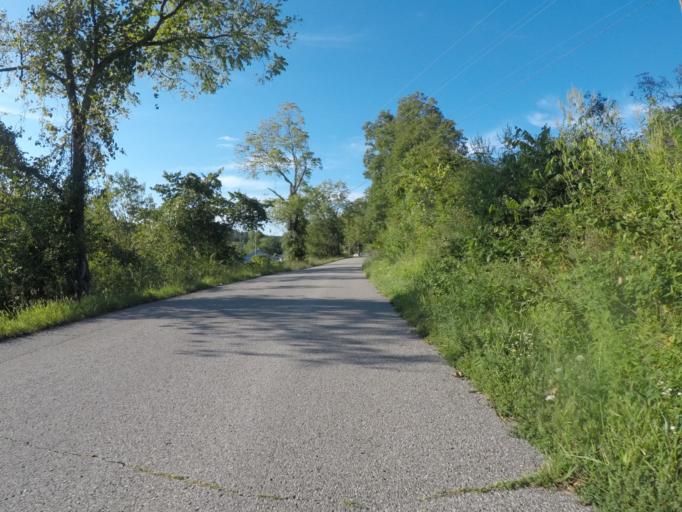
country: US
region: West Virginia
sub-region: Cabell County
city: Huntington
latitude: 38.5169
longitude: -82.5009
